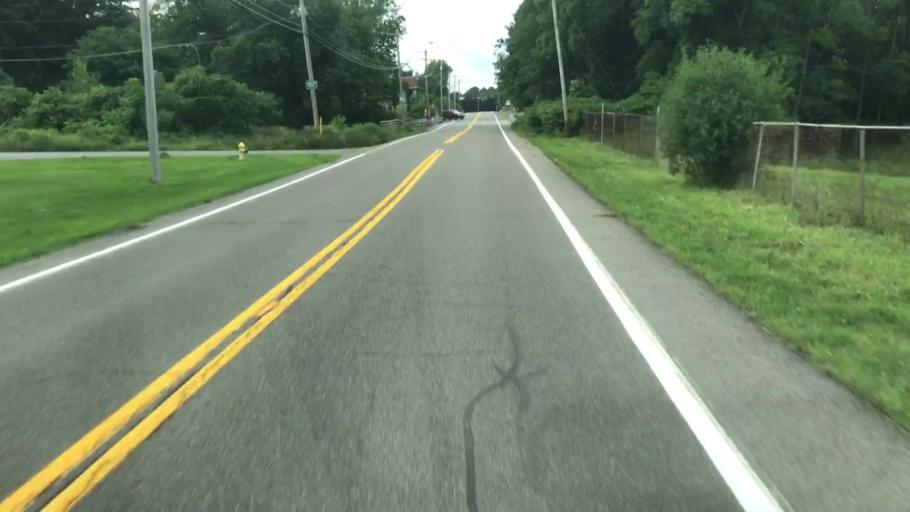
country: US
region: New York
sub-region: Onondaga County
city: Elbridge
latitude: 42.9909
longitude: -76.4536
